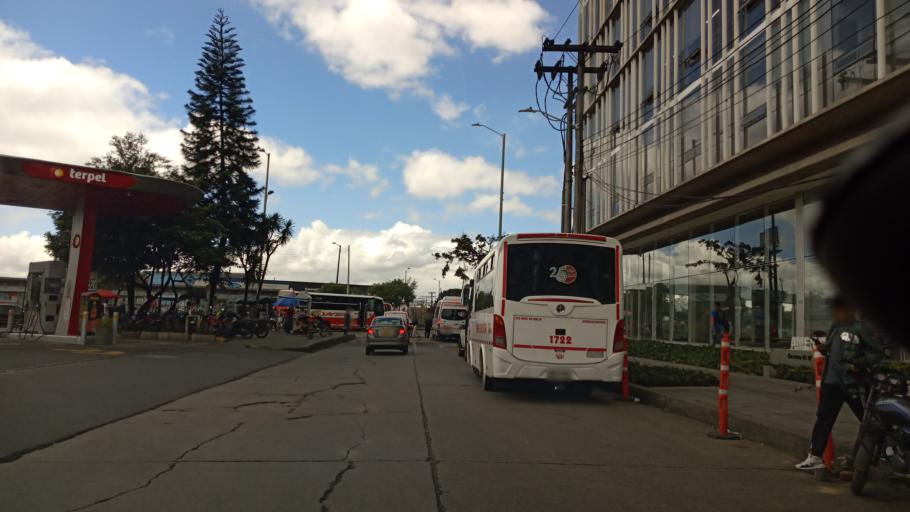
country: CO
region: Bogota D.C.
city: Bogota
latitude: 4.6290
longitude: -74.1117
